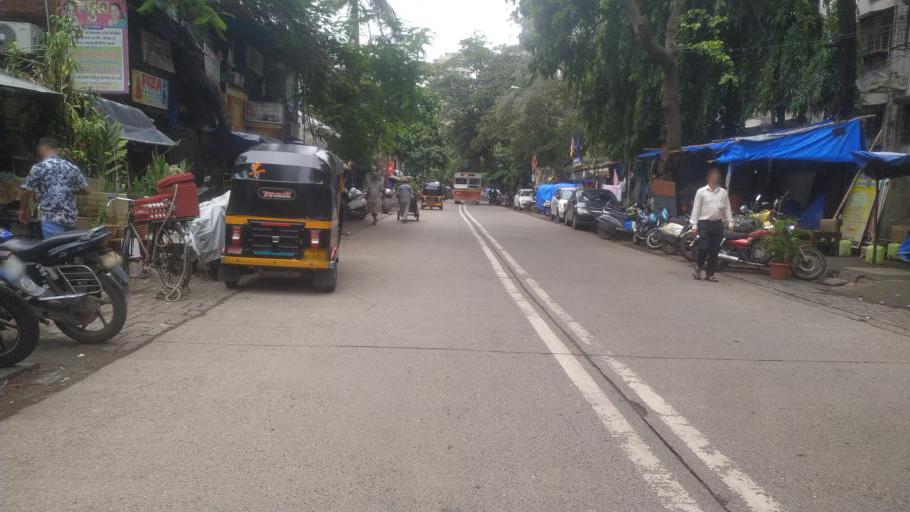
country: IN
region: Maharashtra
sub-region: Mumbai Suburban
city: Mumbai
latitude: 19.0671
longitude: 72.8300
